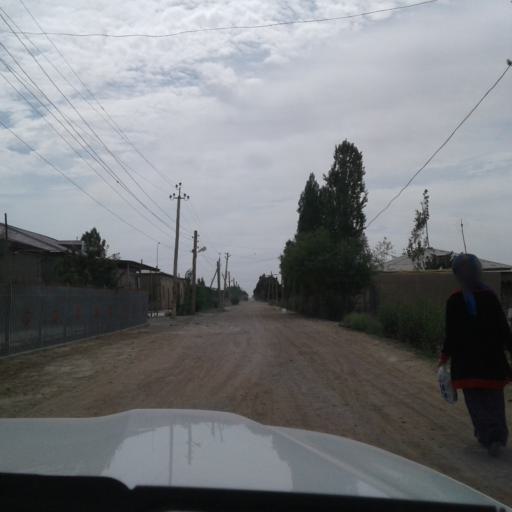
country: TM
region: Dasoguz
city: Tagta
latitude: 41.6005
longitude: 59.8496
